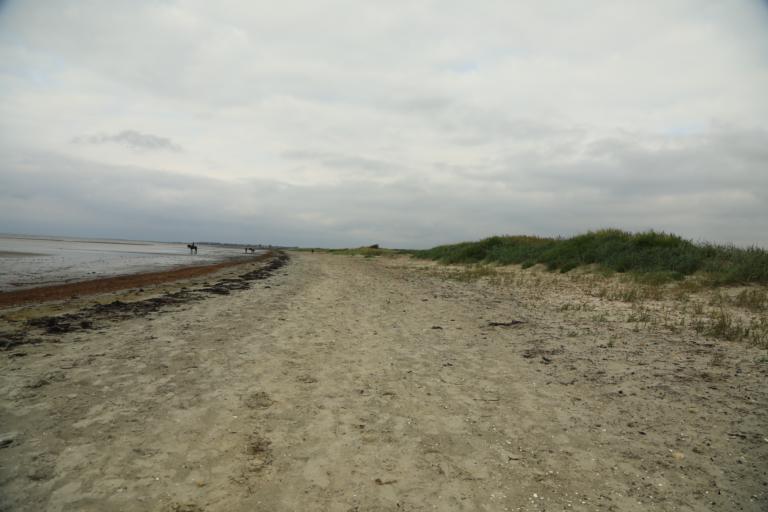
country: SE
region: Halland
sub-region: Varbergs Kommun
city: Tvaaker
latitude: 57.0055
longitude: 12.3502
